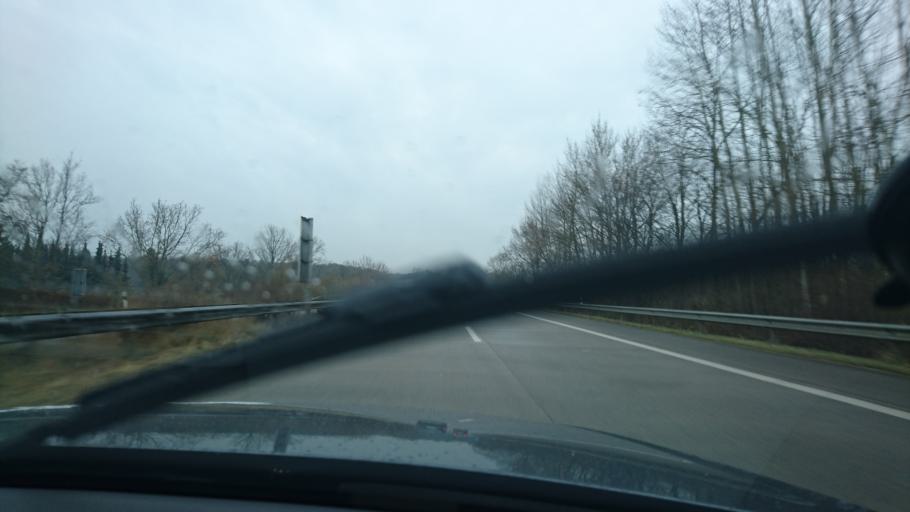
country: DE
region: Schleswig-Holstein
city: Scharbeutz
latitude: 54.0405
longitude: 10.7284
